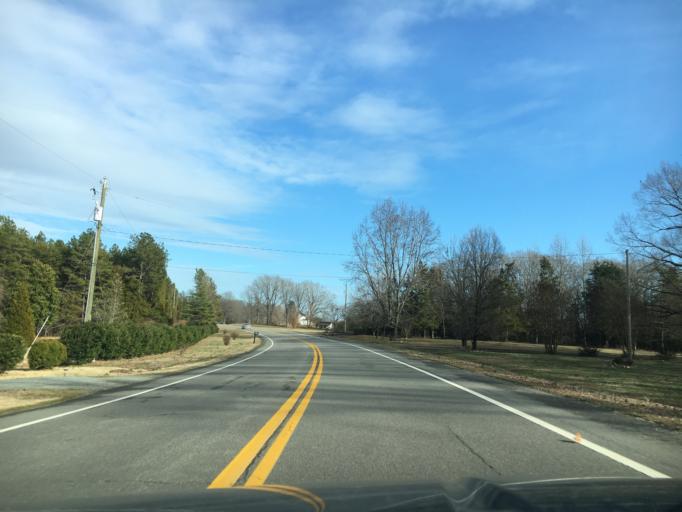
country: US
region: Virginia
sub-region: Halifax County
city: South Boston
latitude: 36.7350
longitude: -78.8533
